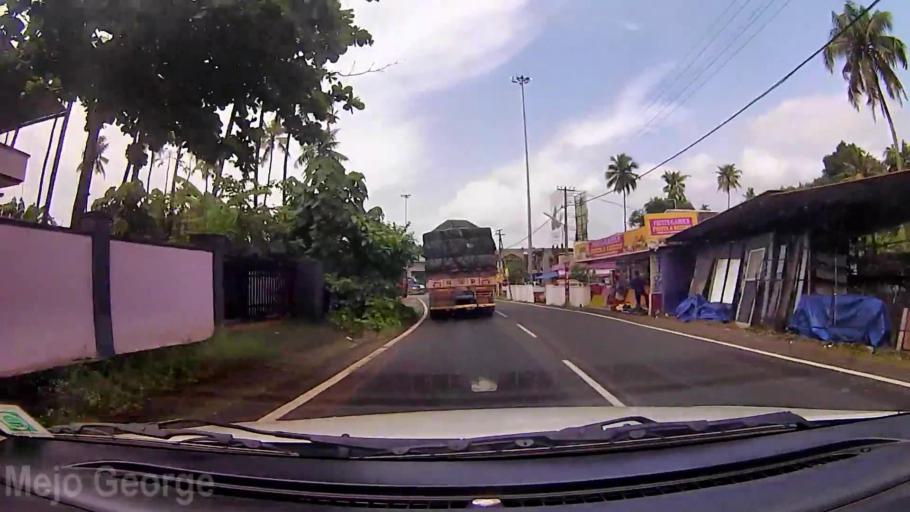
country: IN
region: Kerala
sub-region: Thrissur District
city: Kizhake Chalakudi
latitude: 10.3320
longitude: 76.3079
